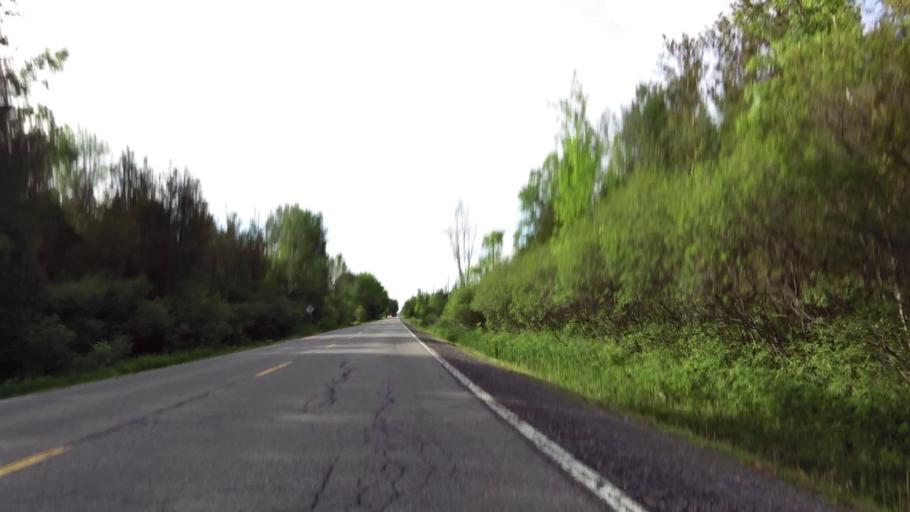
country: CA
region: Ontario
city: Ottawa
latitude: 45.2082
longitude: -75.5959
